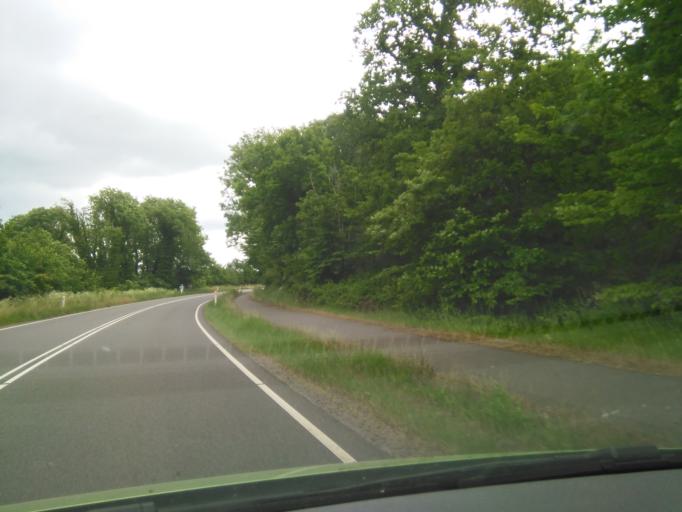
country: DK
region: Capital Region
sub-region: Bornholm Kommune
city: Akirkeby
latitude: 55.2376
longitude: 14.8724
